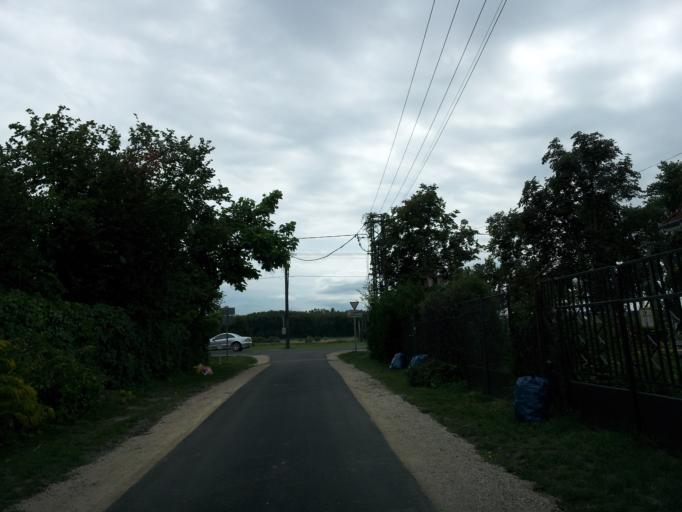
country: HU
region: Somogy
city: Zamardi
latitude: 46.8808
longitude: 17.9260
